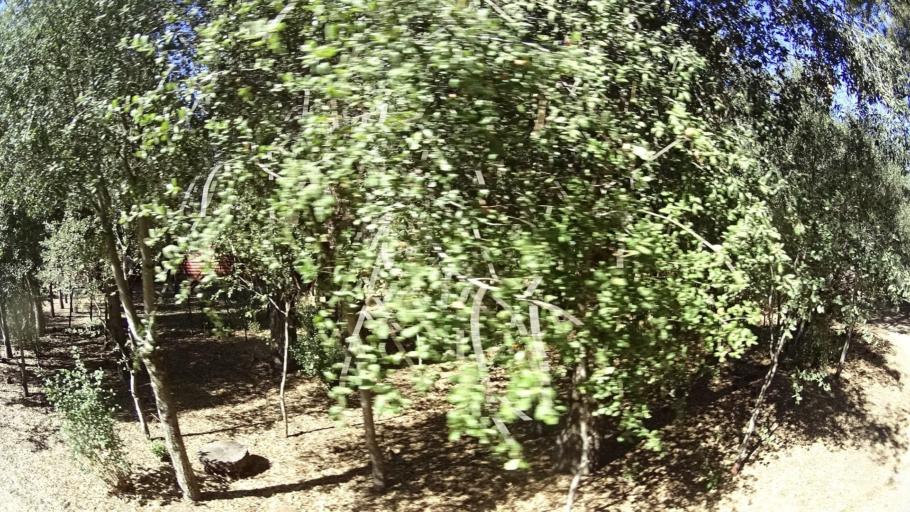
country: US
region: California
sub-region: San Diego County
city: Descanso
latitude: 32.8720
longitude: -116.6213
